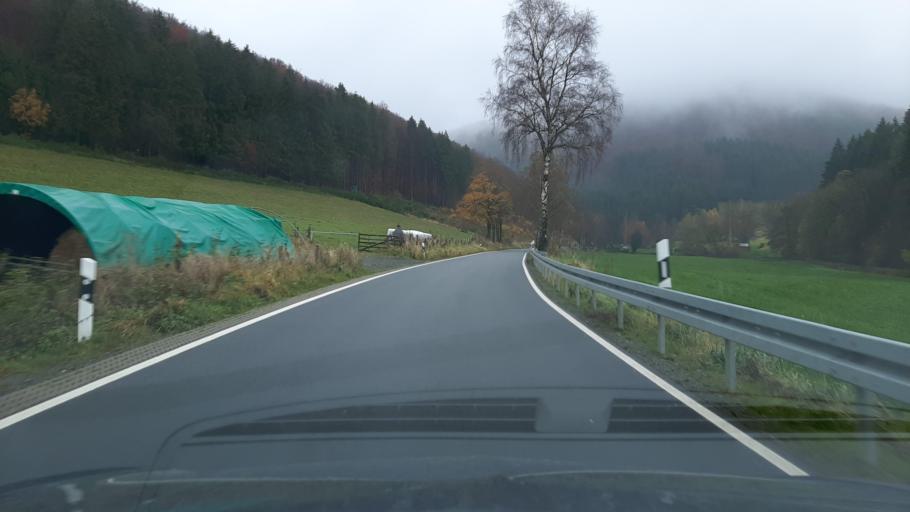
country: DE
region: North Rhine-Westphalia
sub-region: Regierungsbezirk Arnsberg
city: Bad Fredeburg
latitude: 51.1770
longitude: 8.3673
